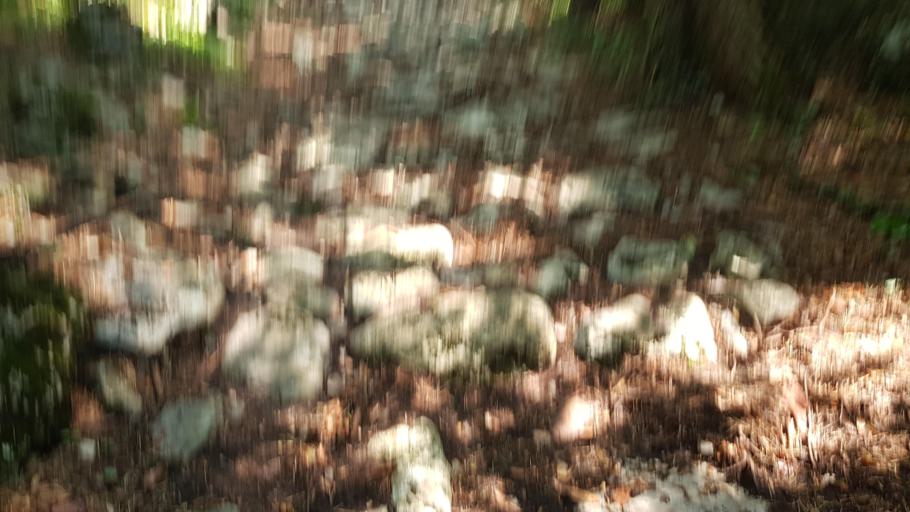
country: IT
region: Trentino-Alto Adige
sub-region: Provincia di Trento
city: Calavino
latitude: 46.0371
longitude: 10.9904
